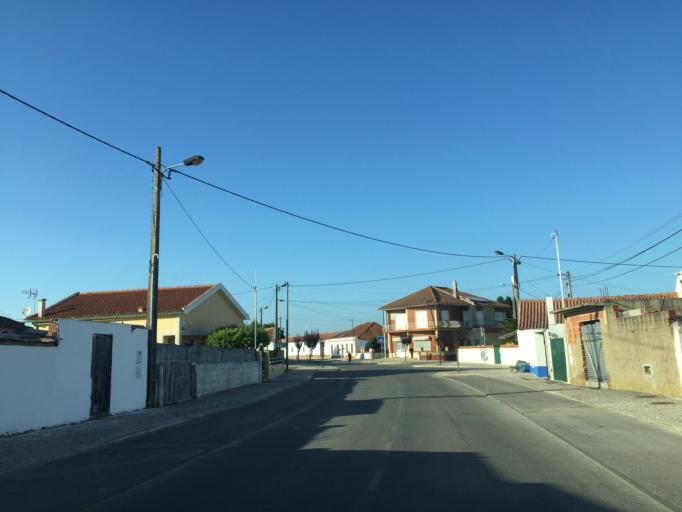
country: PT
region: Lisbon
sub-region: Azambuja
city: Aveiras de Cima
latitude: 39.1367
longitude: -8.9228
